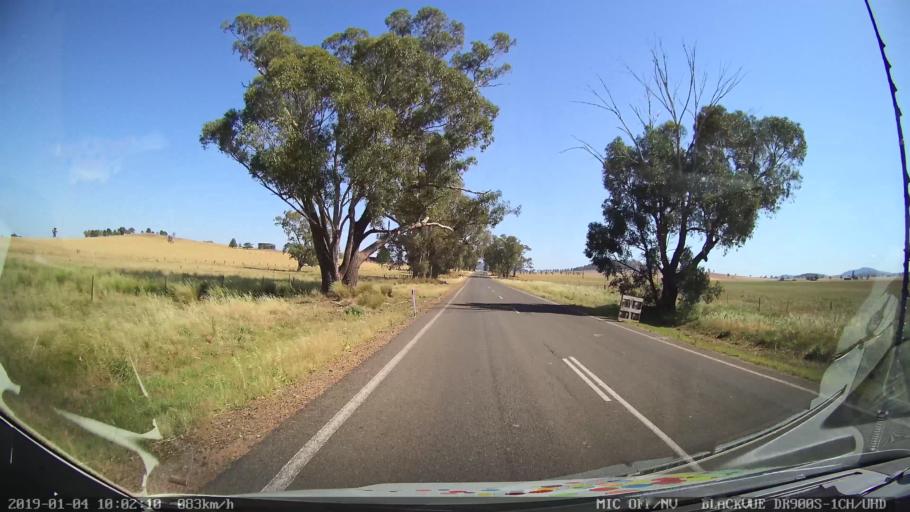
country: AU
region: New South Wales
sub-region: Cabonne
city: Canowindra
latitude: -33.4797
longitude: 148.3660
